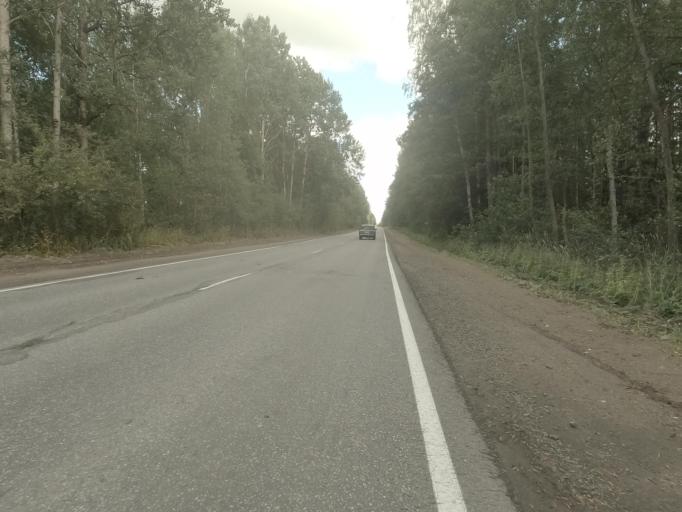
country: RU
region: Leningrad
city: Romanovka
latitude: 60.0211
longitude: 30.7265
